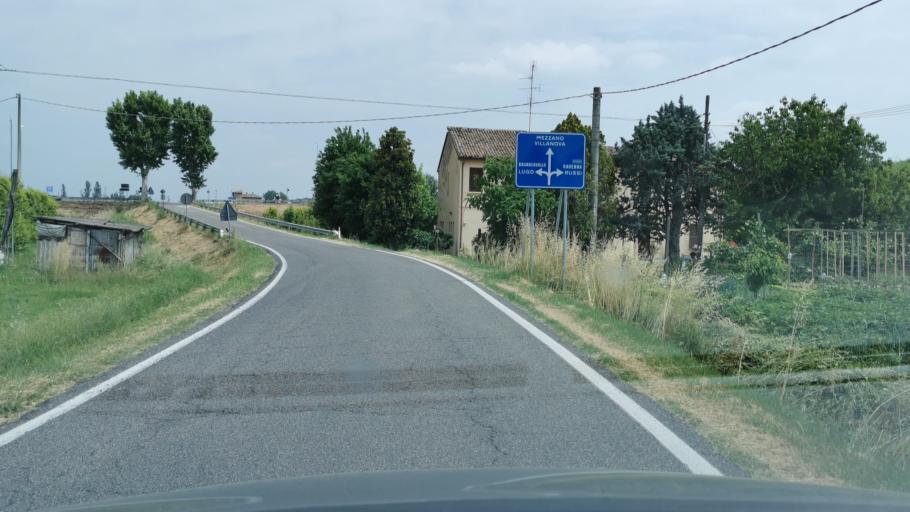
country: IT
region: Emilia-Romagna
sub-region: Provincia di Ravenna
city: Russi
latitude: 44.4006
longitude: 12.0212
